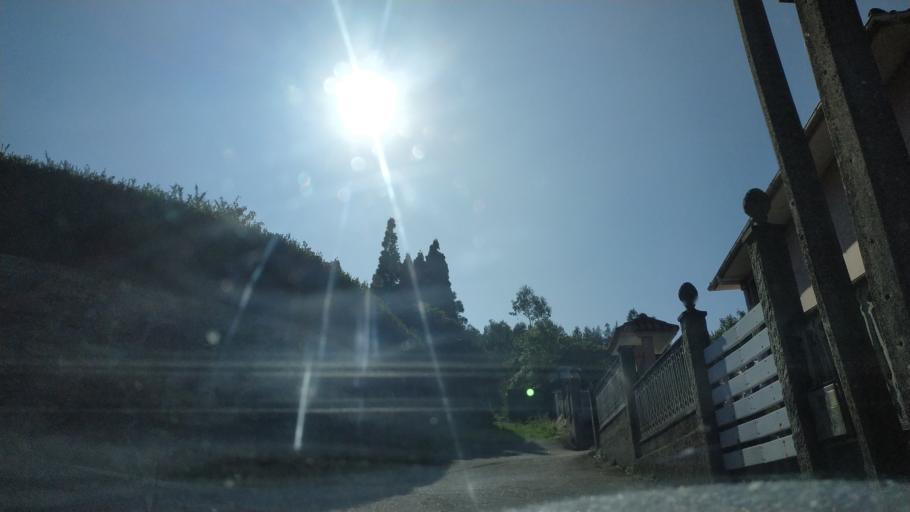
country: ES
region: Galicia
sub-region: Provincia da Coruna
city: Culleredo
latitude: 43.3261
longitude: -8.3898
